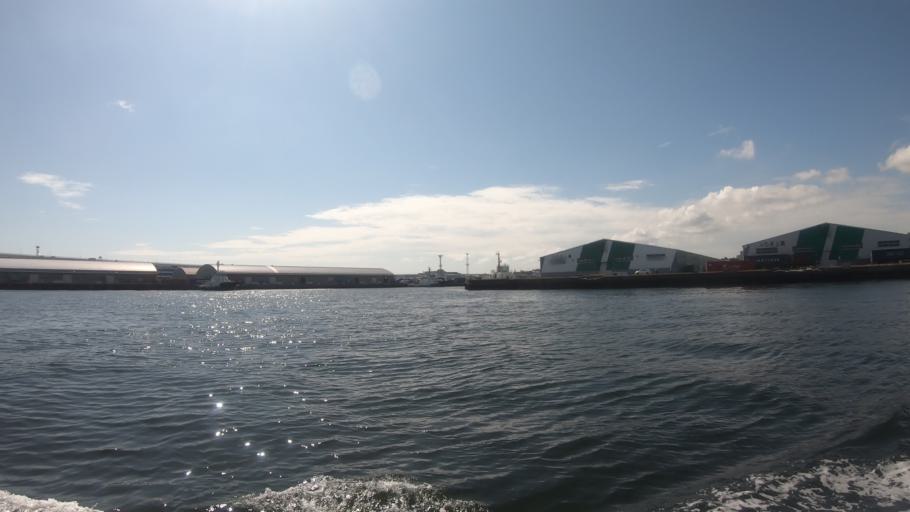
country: JP
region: Kanagawa
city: Yokohama
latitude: 35.4507
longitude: 139.6614
